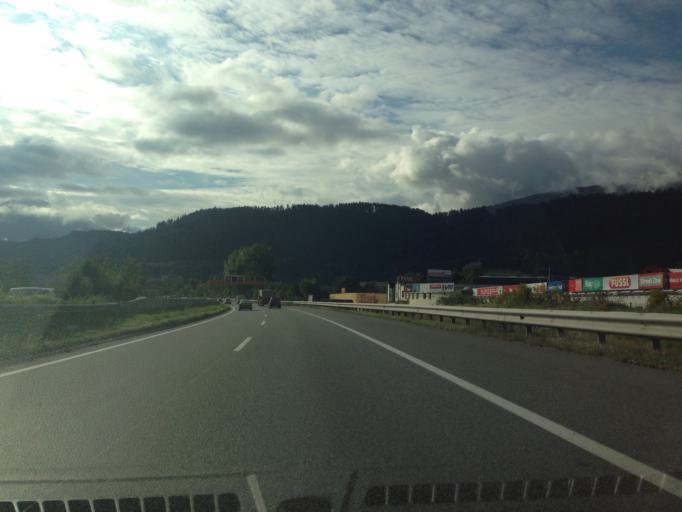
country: AT
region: Tyrol
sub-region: Politischer Bezirk Innsbruck Land
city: Vols
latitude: 47.2575
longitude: 11.3258
